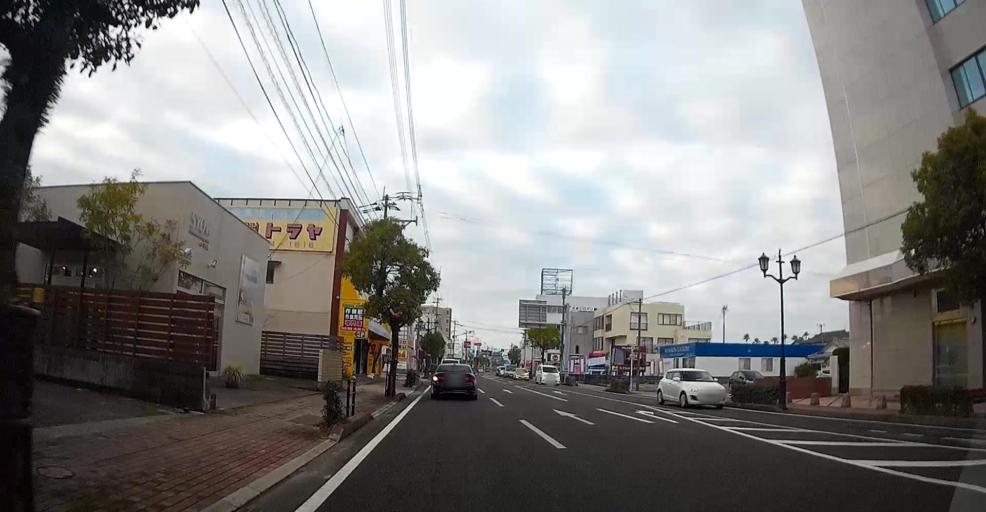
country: JP
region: Kumamoto
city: Hondo
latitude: 32.4512
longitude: 130.1973
